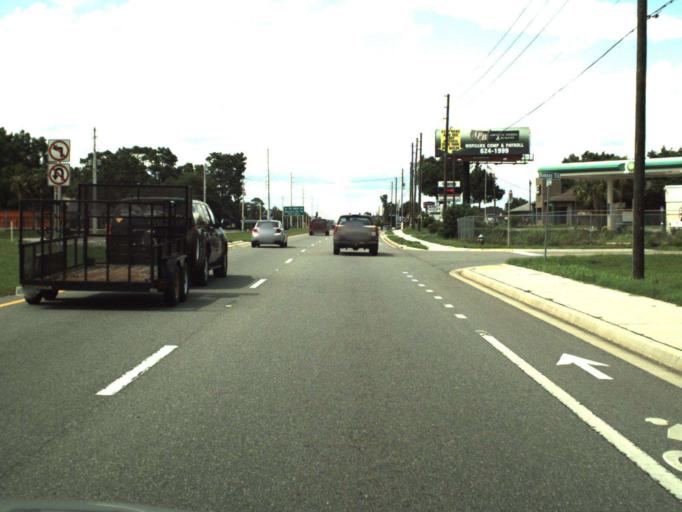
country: US
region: Florida
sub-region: Marion County
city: Silver Springs Shores
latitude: 29.1573
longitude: -82.0536
